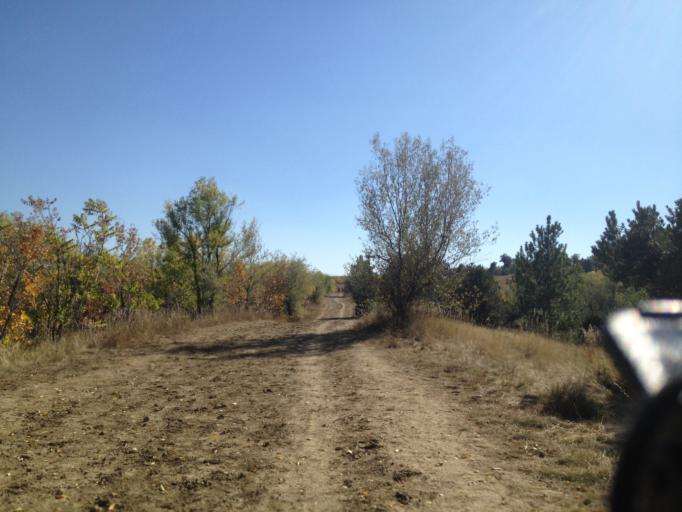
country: US
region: Colorado
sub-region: Boulder County
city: Boulder
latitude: 39.9811
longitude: -105.2354
